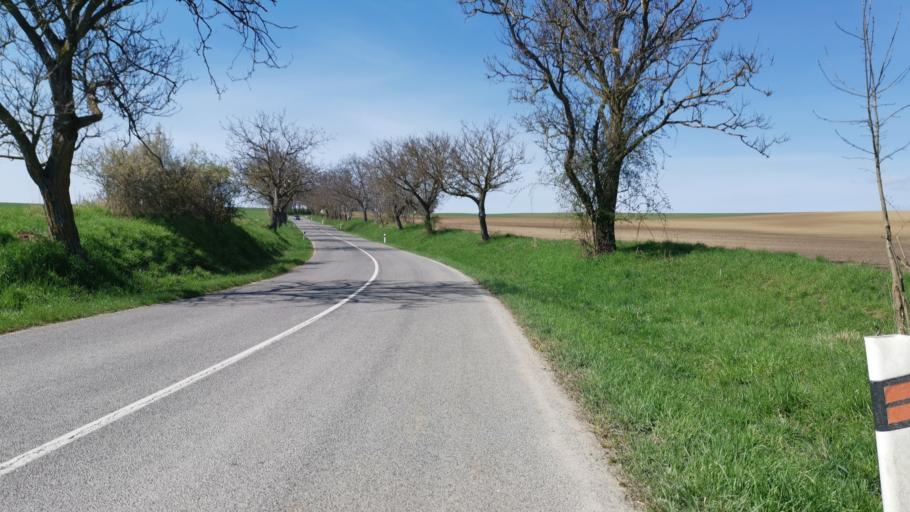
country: SK
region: Trnavsky
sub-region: Okres Skalica
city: Holic
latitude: 48.7364
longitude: 17.2074
